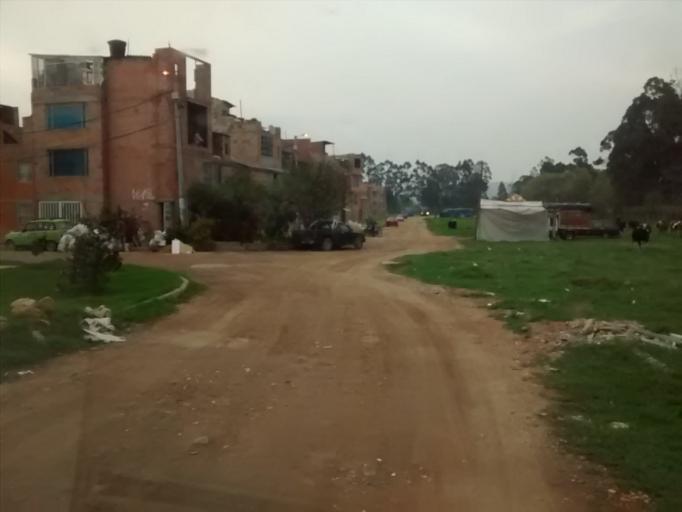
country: CO
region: Cundinamarca
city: Cota
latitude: 4.7590
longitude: -74.1130
